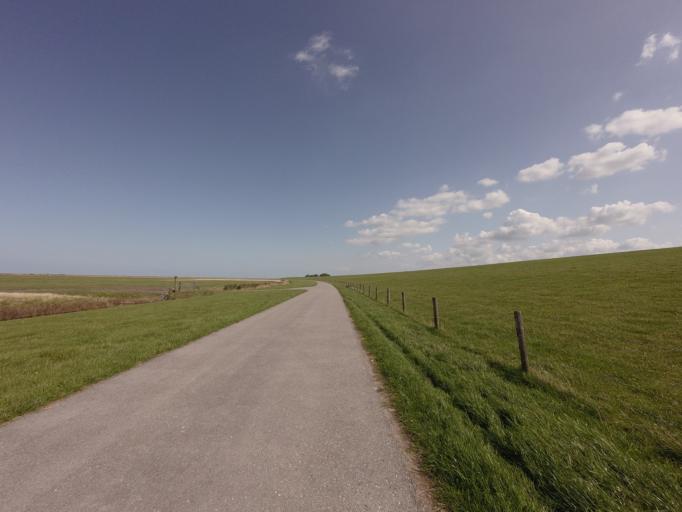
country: NL
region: Friesland
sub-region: Gemeente Ferwerderadiel
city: Marrum
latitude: 53.3441
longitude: 5.7972
